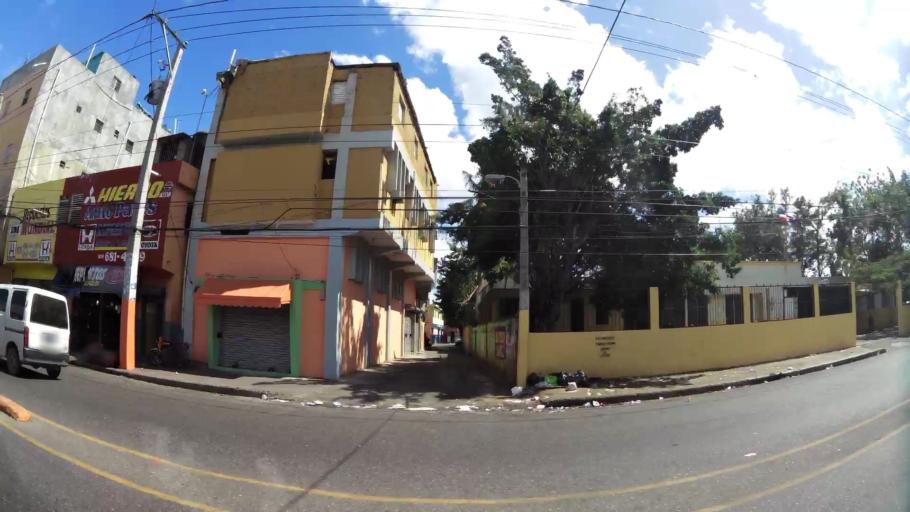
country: DO
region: Nacional
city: Ensanche Luperon
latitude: 18.4940
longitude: -69.8998
